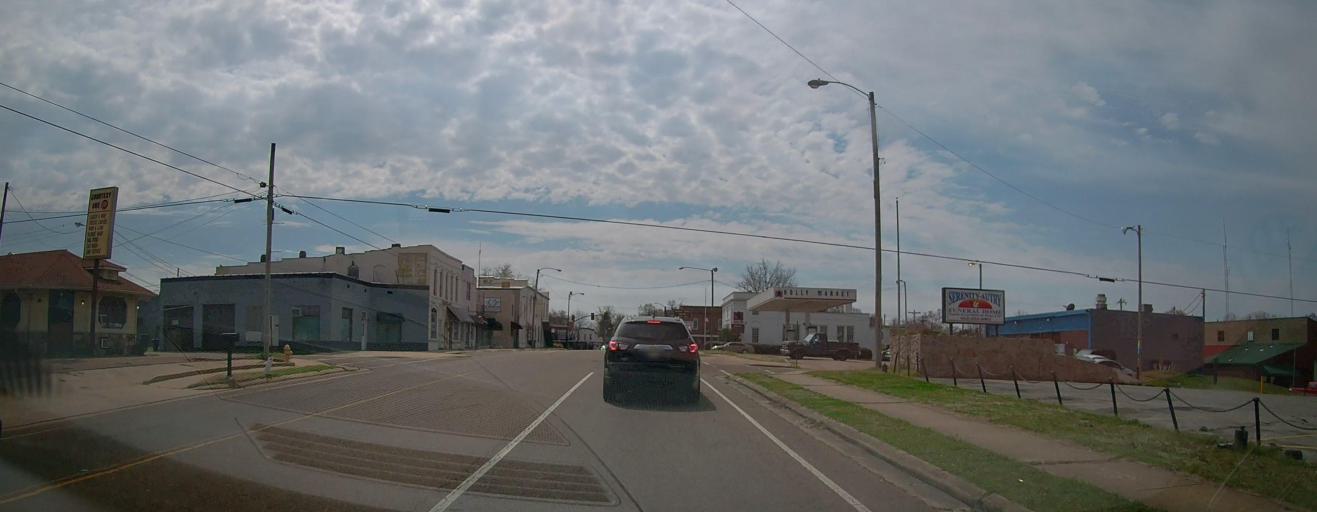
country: US
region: Mississippi
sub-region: Marshall County
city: Holly Springs
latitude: 34.7698
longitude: -89.4487
